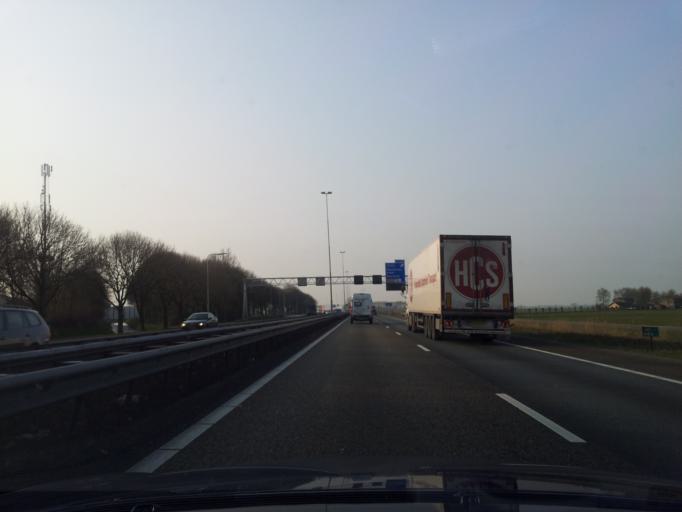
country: NL
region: Utrecht
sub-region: Gemeente Lopik
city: Lopik
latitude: 51.9153
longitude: 4.9863
